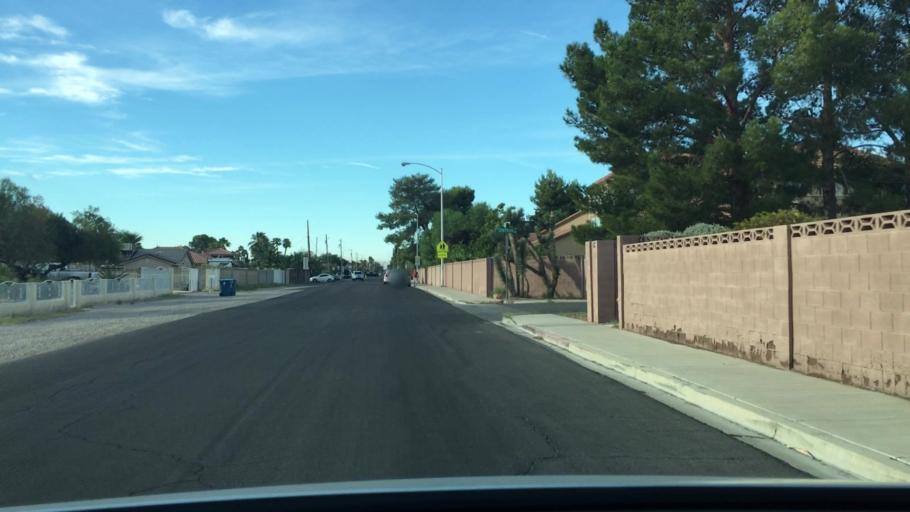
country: US
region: Nevada
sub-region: Clark County
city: Spring Valley
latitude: 36.1323
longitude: -115.2230
